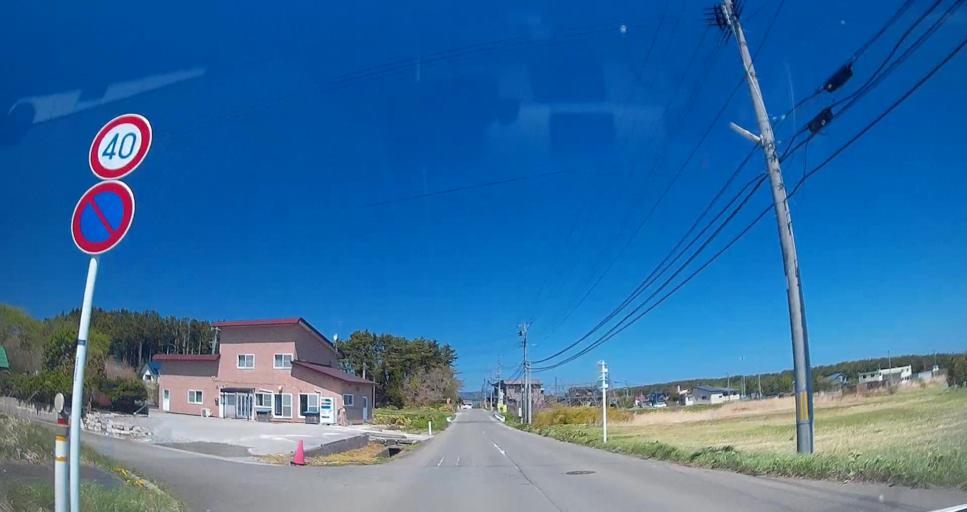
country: JP
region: Aomori
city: Mutsu
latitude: 41.2302
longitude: 141.3980
